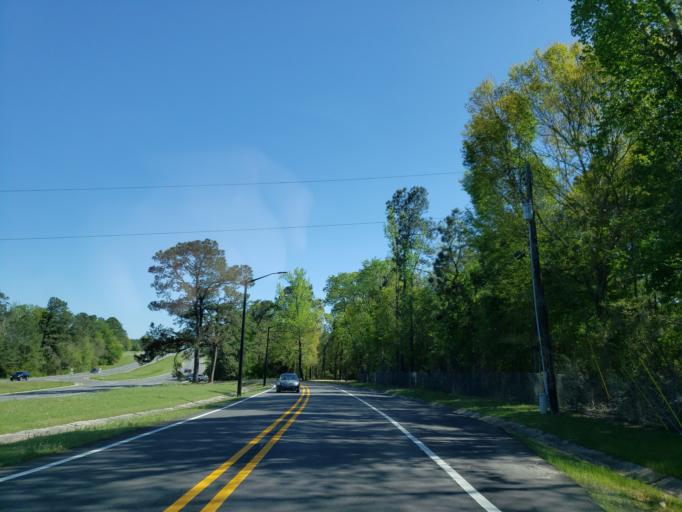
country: US
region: Mississippi
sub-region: Stone County
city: Wiggins
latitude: 30.8660
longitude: -89.1655
